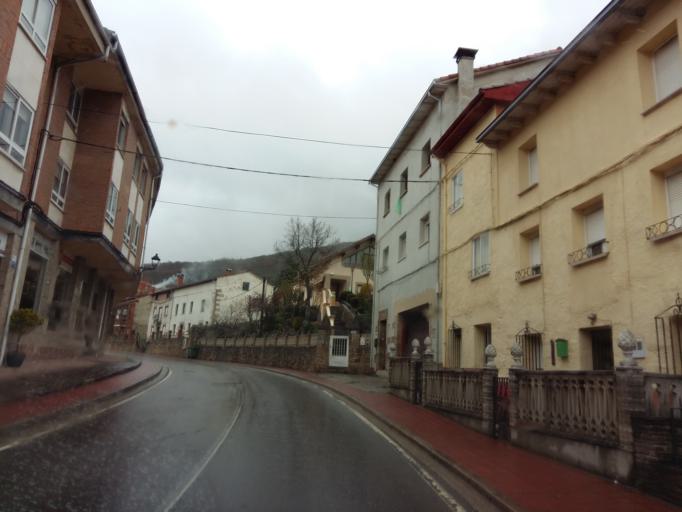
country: ES
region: Castille and Leon
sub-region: Provincia de Palencia
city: Barruelo de Santullan
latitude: 42.9103
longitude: -4.2881
